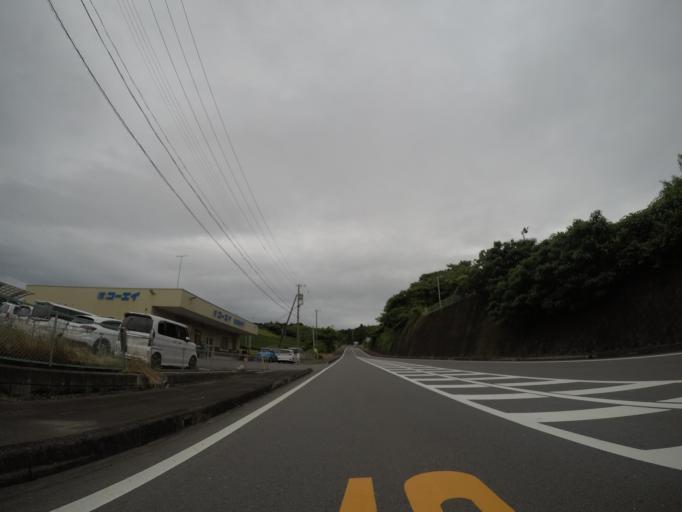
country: JP
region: Shizuoka
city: Sagara
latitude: 34.7267
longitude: 138.1638
